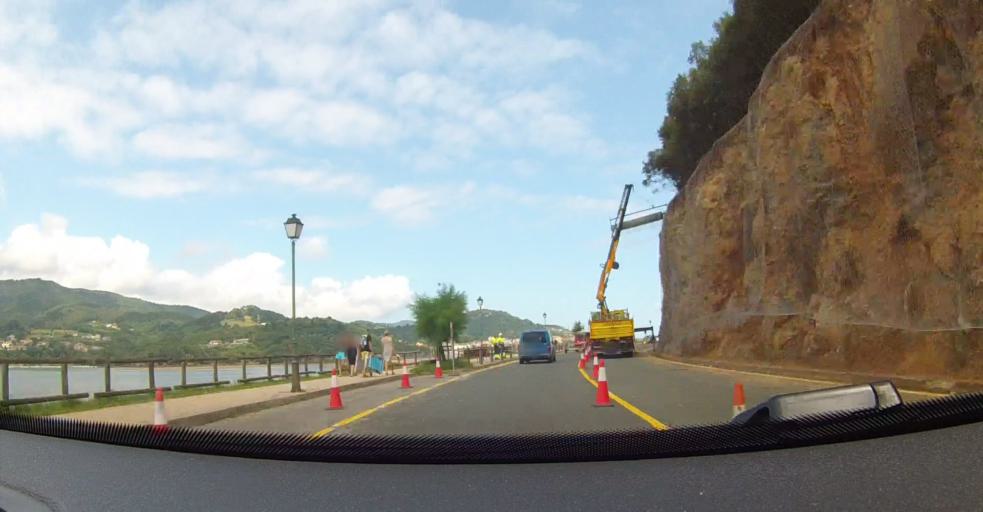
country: ES
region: Basque Country
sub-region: Bizkaia
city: Mundaka
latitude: 43.3968
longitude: -2.6838
